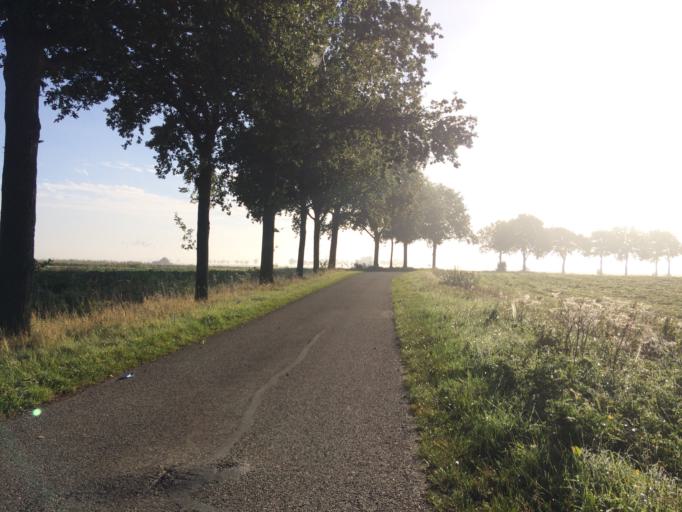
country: NL
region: Gelderland
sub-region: Gemeente Zaltbommel
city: Nederhemert-Noord
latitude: 51.7297
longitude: 5.2054
